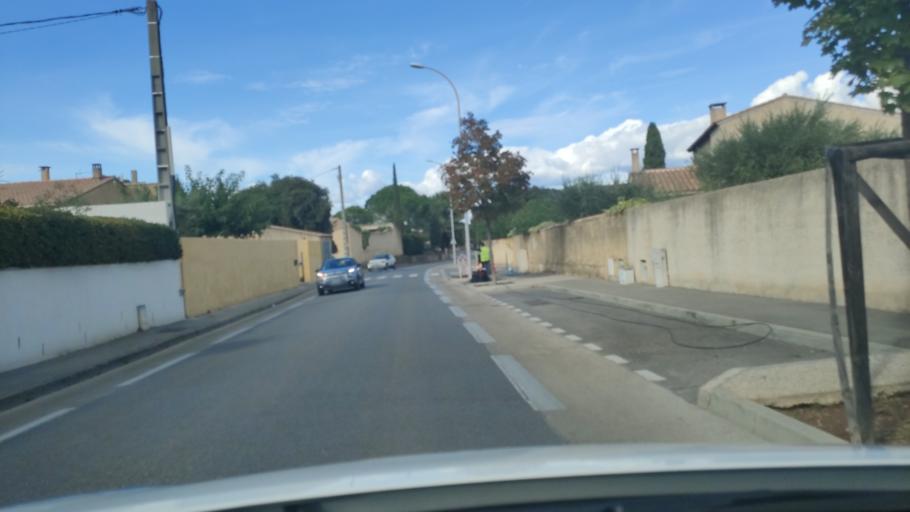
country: FR
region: Languedoc-Roussillon
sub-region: Departement du Gard
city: Villeneuve-les-Avignon
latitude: 43.9714
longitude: 4.7805
